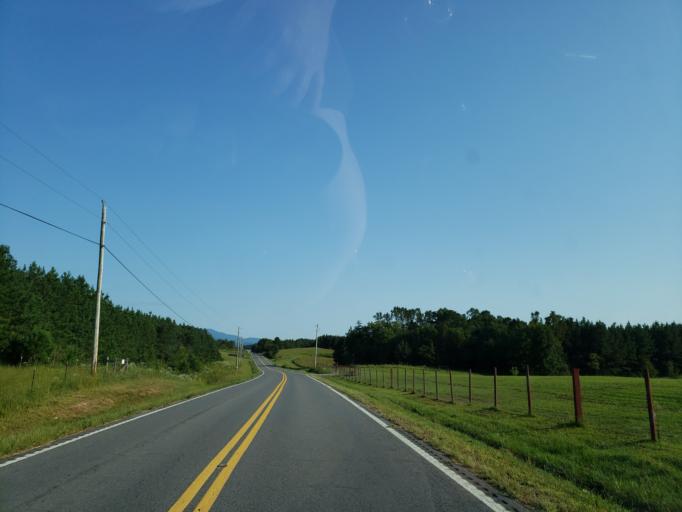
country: US
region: Tennessee
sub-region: Bradley County
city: Wildwood Lake
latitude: 35.0242
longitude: -84.7961
